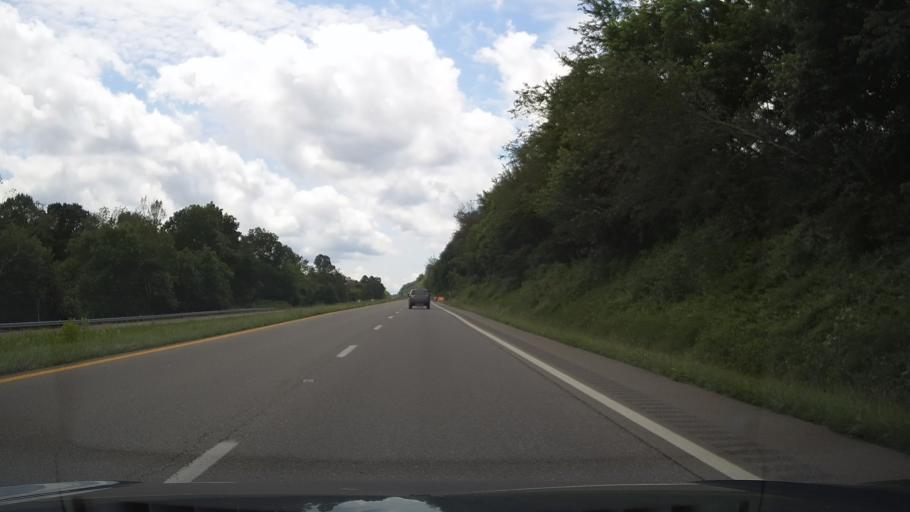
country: US
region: Virginia
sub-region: Scott County
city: Gate City
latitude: 36.6382
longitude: -82.6624
